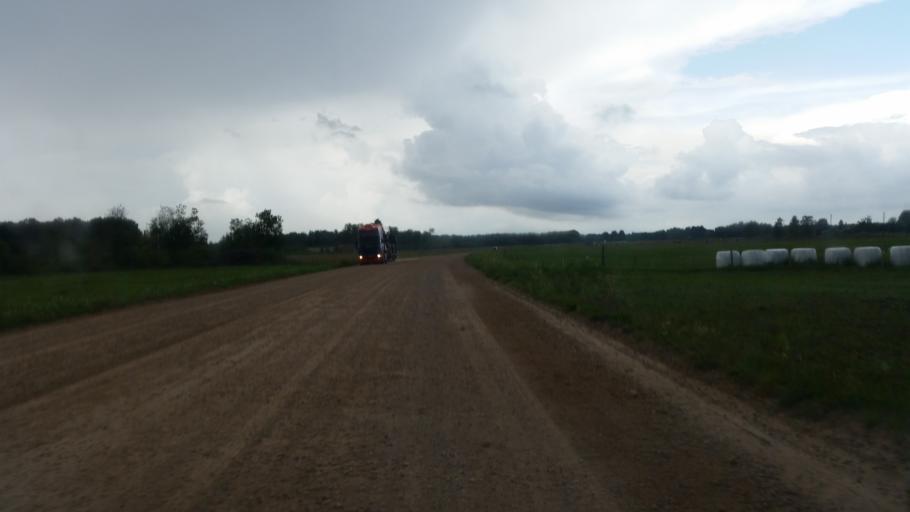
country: LV
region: Vecumnieki
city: Vecumnieki
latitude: 56.4261
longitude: 24.4732
